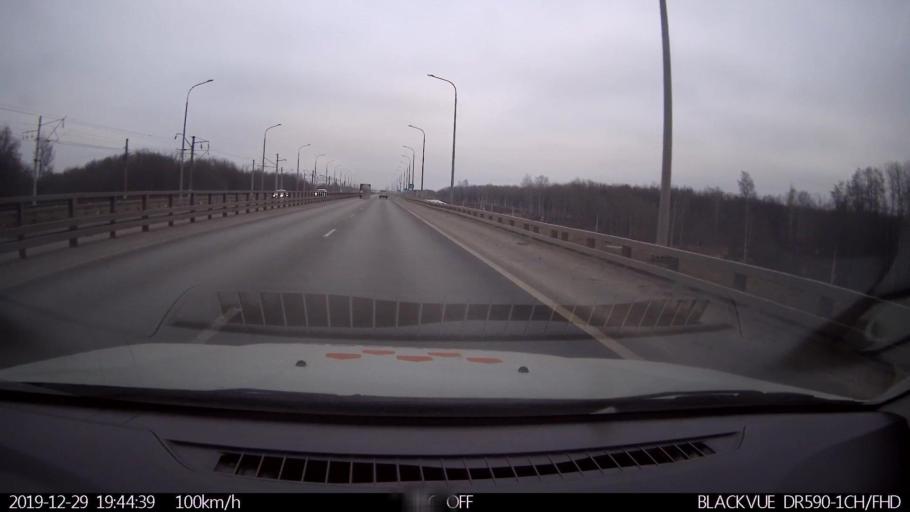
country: RU
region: Nizjnij Novgorod
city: Neklyudovo
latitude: 56.3779
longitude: 43.9542
